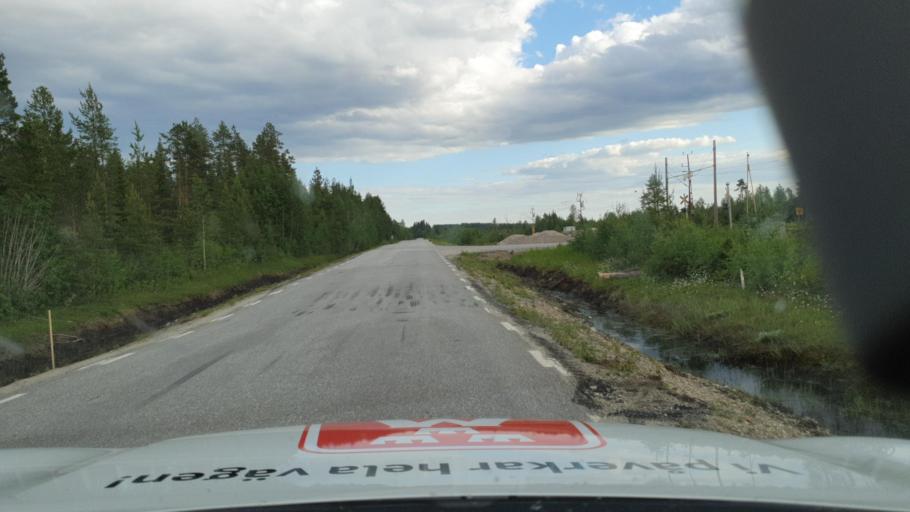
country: SE
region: Vaesterbotten
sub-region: Vindelns Kommun
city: Vindeln
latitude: 64.3416
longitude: 19.6238
